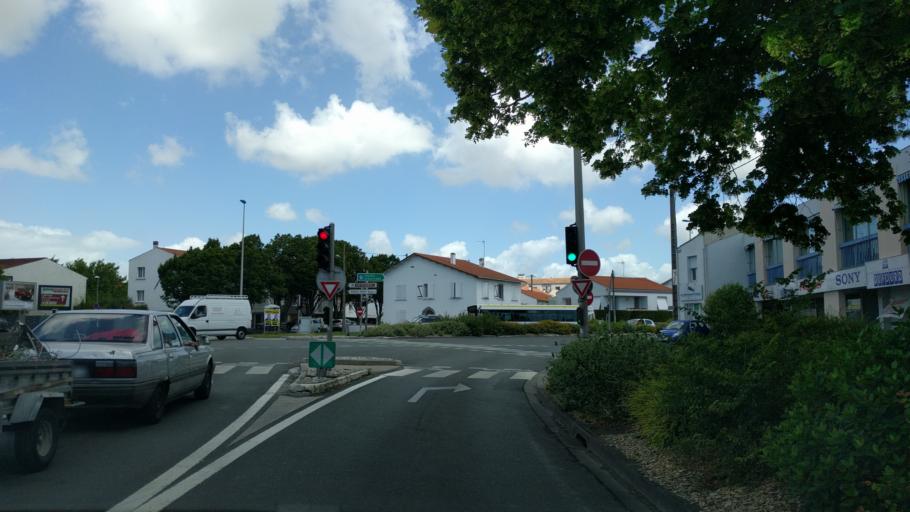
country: FR
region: Poitou-Charentes
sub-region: Departement de la Charente-Maritime
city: La Rochelle
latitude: 46.1662
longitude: -1.1368
